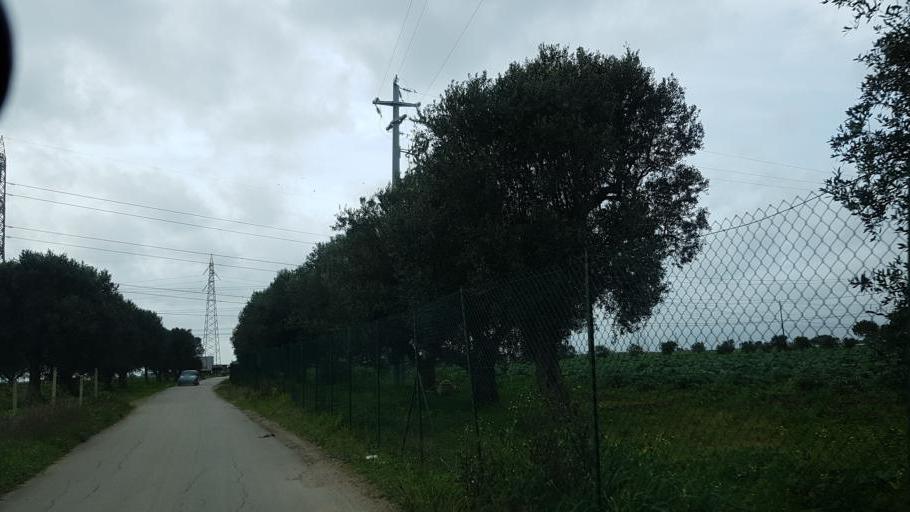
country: IT
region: Apulia
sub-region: Provincia di Brindisi
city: La Rosa
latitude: 40.6008
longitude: 17.9219
